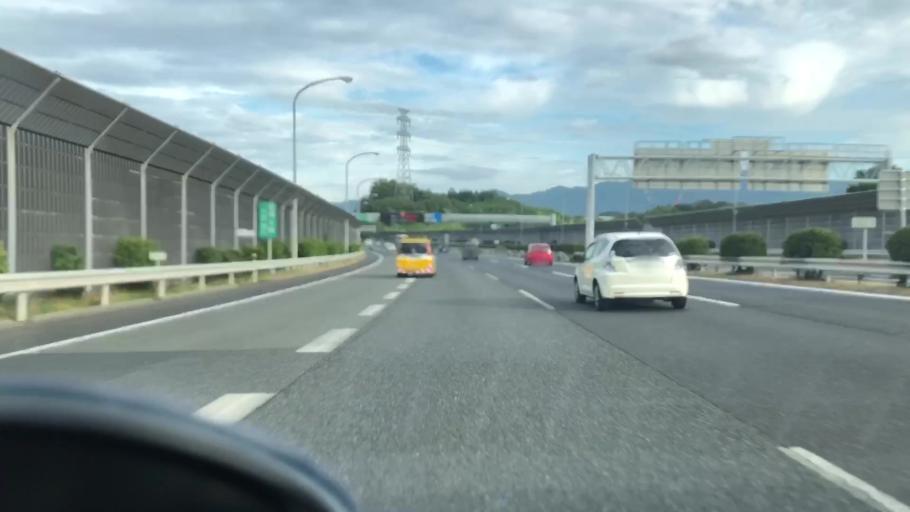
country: JP
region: Hyogo
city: Sandacho
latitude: 34.8418
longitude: 135.2287
